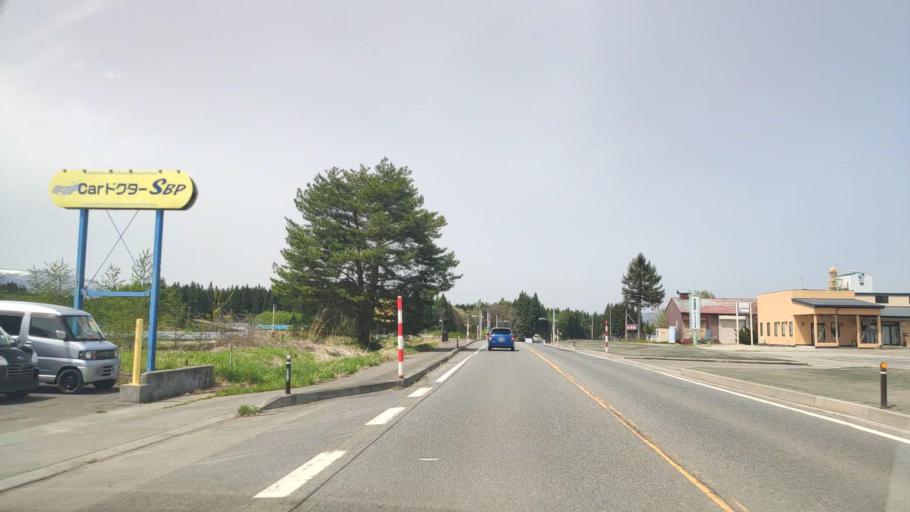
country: JP
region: Aomori
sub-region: Misawa Shi
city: Inuotose
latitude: 40.6765
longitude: 141.1748
